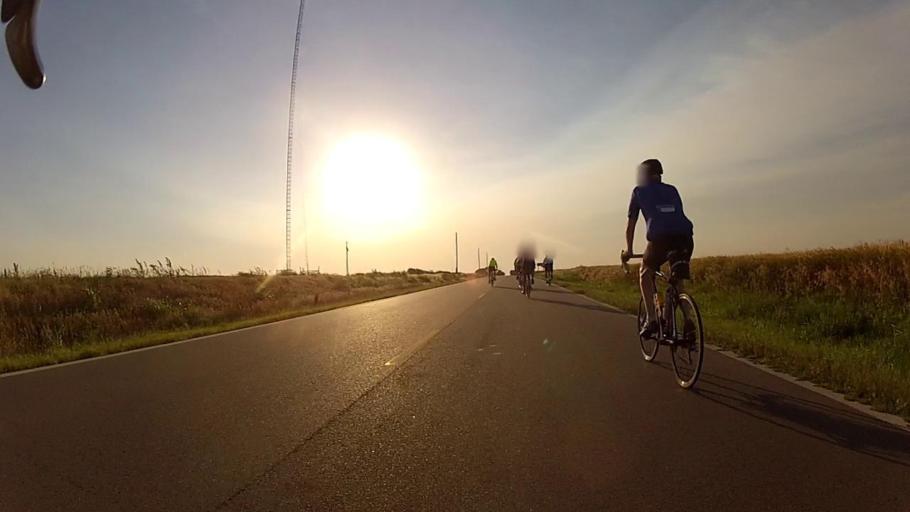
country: US
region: Kansas
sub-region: Harper County
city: Anthony
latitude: 37.1537
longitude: -97.8594
